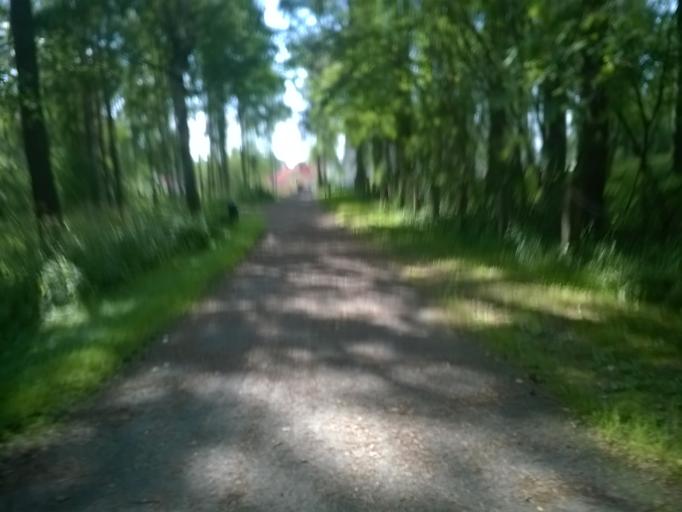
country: FI
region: Kainuu
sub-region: Kehys-Kainuu
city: Kuhmo
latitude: 64.1315
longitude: 29.5240
